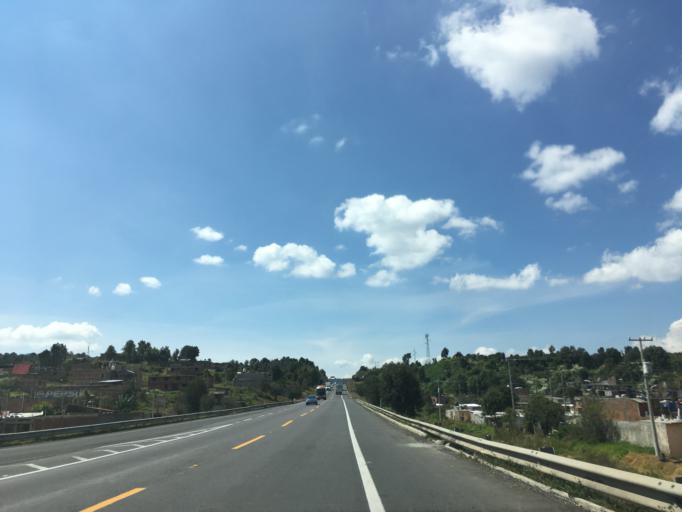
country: MX
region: Michoacan
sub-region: Patzcuaro
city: Colonia Vista Bella (Lomas del Peaje)
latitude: 19.4931
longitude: -101.6040
